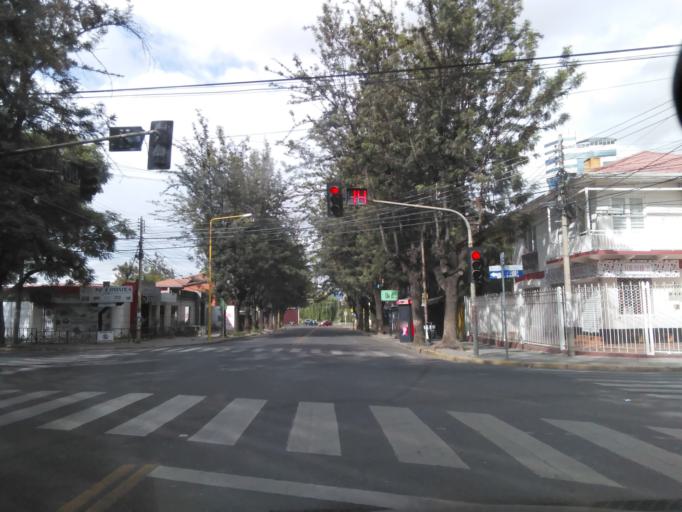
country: BO
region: Cochabamba
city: Cochabamba
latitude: -17.3864
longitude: -66.1546
